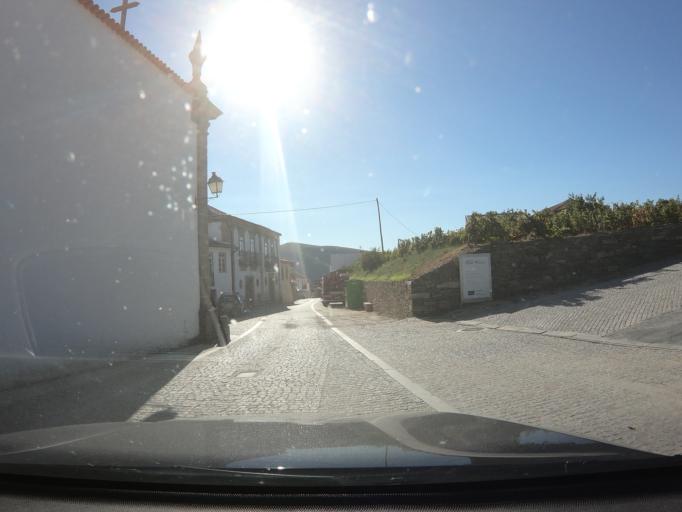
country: PT
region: Vila Real
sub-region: Sabrosa
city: Vilela
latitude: 41.2186
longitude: -7.5638
